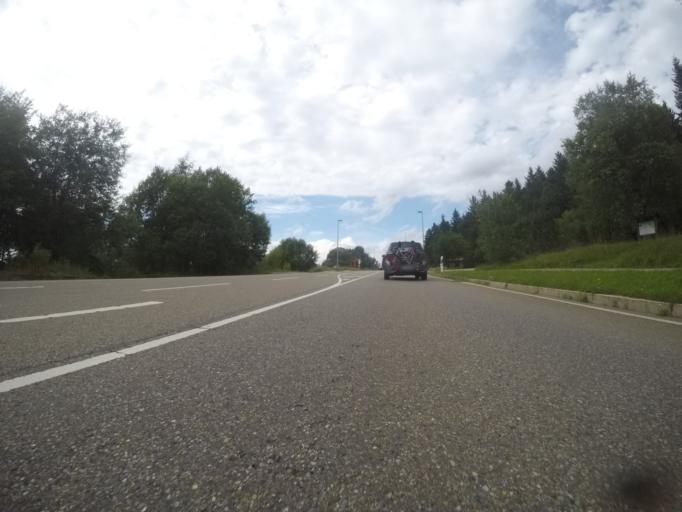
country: DE
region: Baden-Wuerttemberg
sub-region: Karlsruhe Region
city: Bad Rippoldsau-Schapbach
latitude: 48.4735
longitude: 8.2969
